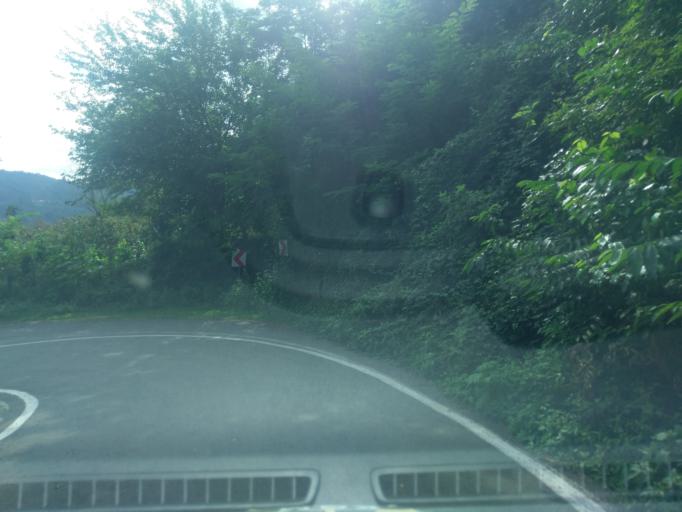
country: TR
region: Ordu
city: Camas
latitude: 40.9272
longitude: 37.6197
